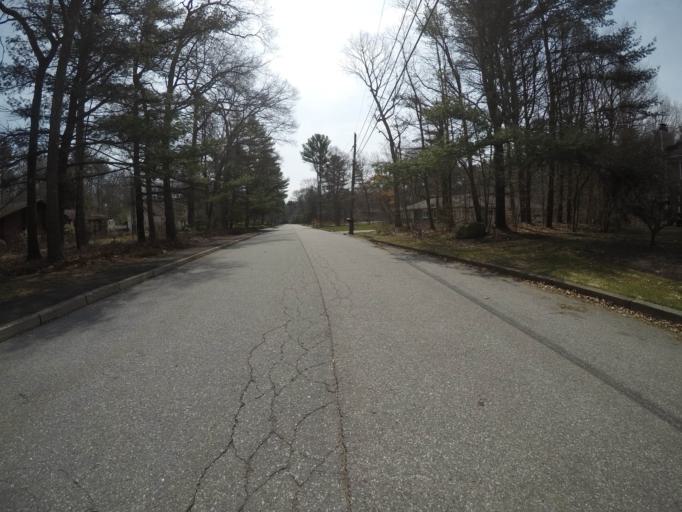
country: US
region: Massachusetts
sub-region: Bristol County
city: Easton
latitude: 42.0511
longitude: -71.1255
